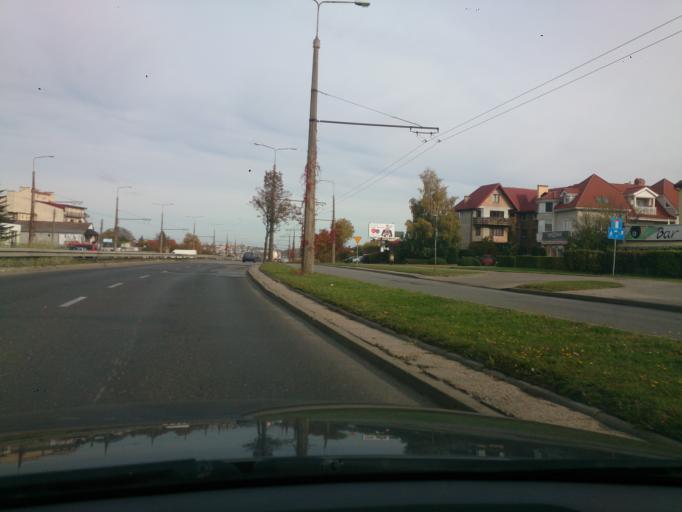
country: PL
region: Pomeranian Voivodeship
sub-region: Gdynia
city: Wielki Kack
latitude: 54.4757
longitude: 18.5170
